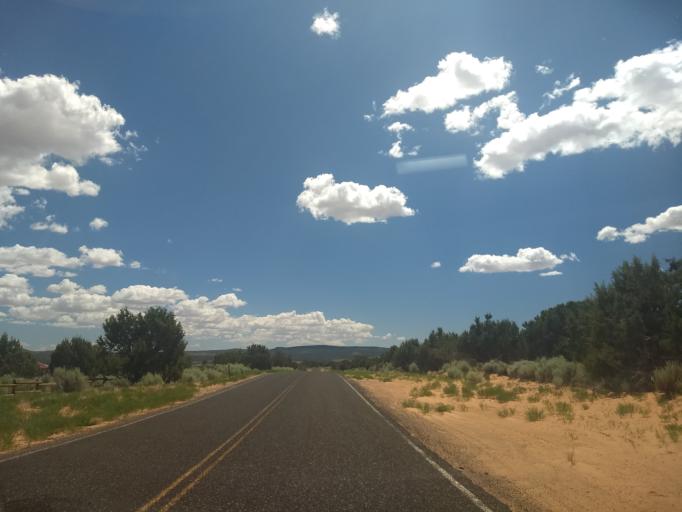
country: US
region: Utah
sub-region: Kane County
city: Kanab
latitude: 37.0398
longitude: -112.7298
